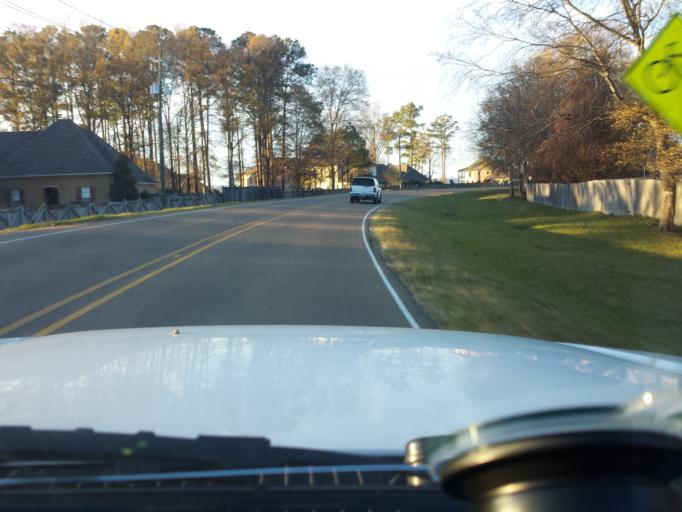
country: US
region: Mississippi
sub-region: Madison County
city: Madison
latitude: 32.4144
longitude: -90.0204
